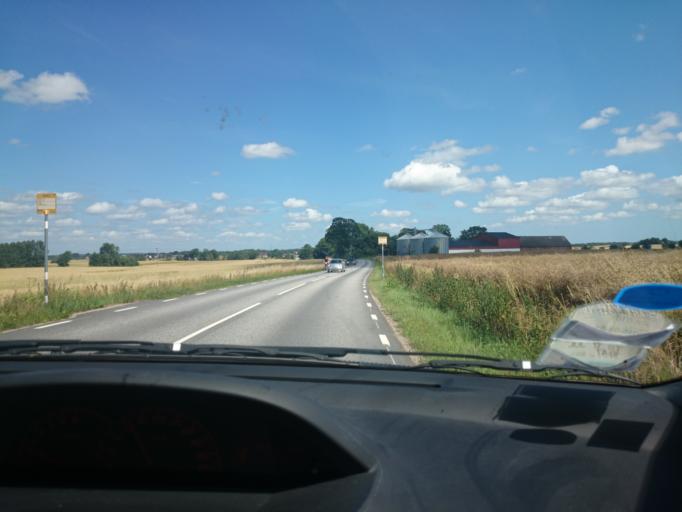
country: SE
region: Skane
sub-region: Tomelilla Kommun
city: Tomelilla
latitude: 55.6368
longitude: 13.8774
